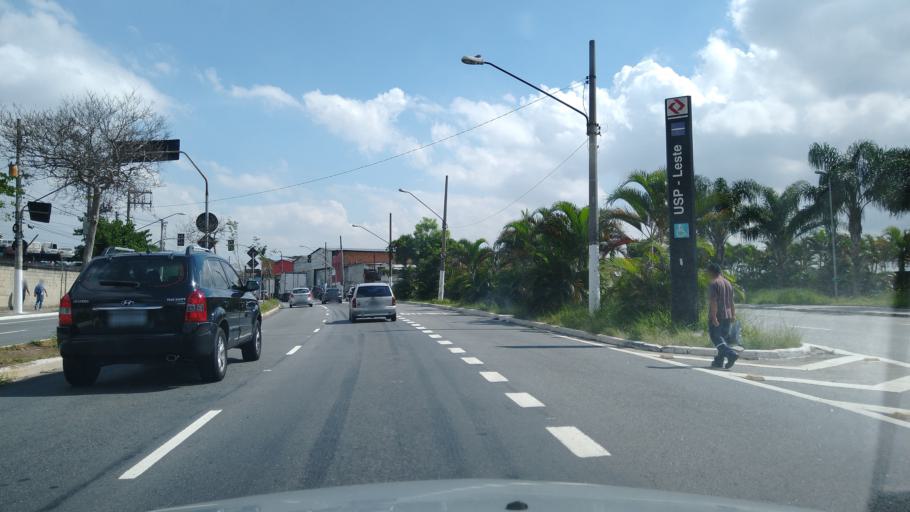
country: BR
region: Sao Paulo
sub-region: Guarulhos
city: Guarulhos
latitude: -23.4859
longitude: -46.5024
